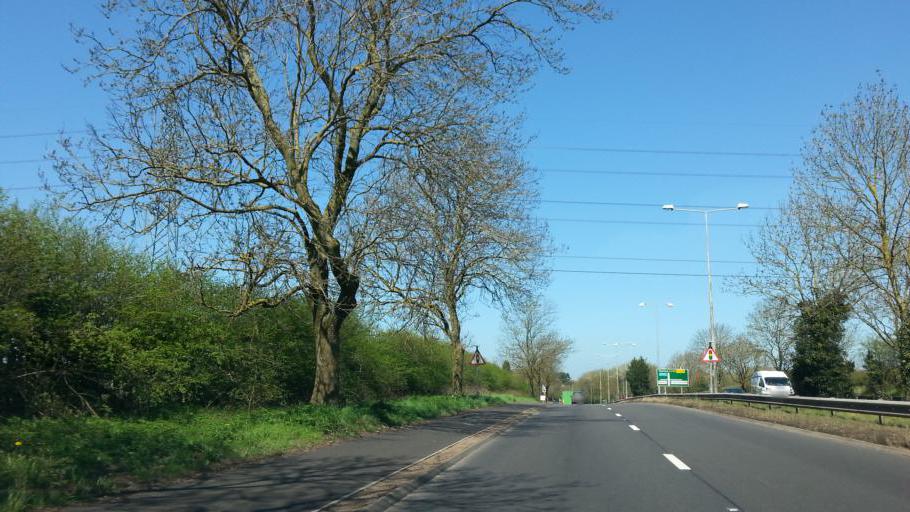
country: GB
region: England
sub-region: Staffordshire
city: Featherstone
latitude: 52.6641
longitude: -2.1318
